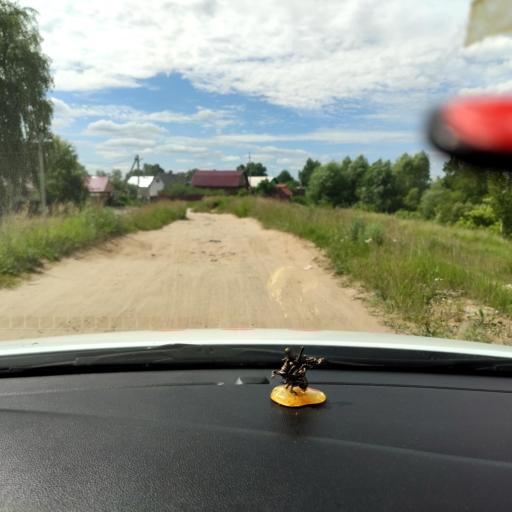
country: RU
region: Tatarstan
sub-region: Zelenodol'skiy Rayon
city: Vasil'yevo
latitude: 55.8360
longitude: 48.7188
